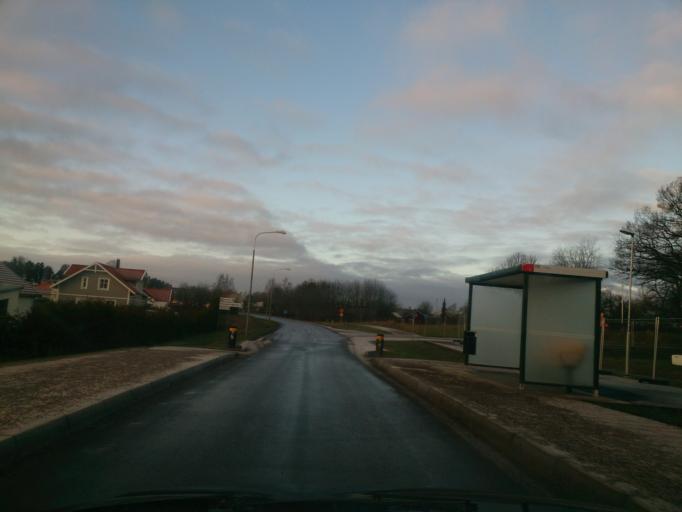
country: SE
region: OEstergoetland
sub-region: Linkopings Kommun
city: Linghem
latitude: 58.4081
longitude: 15.8552
